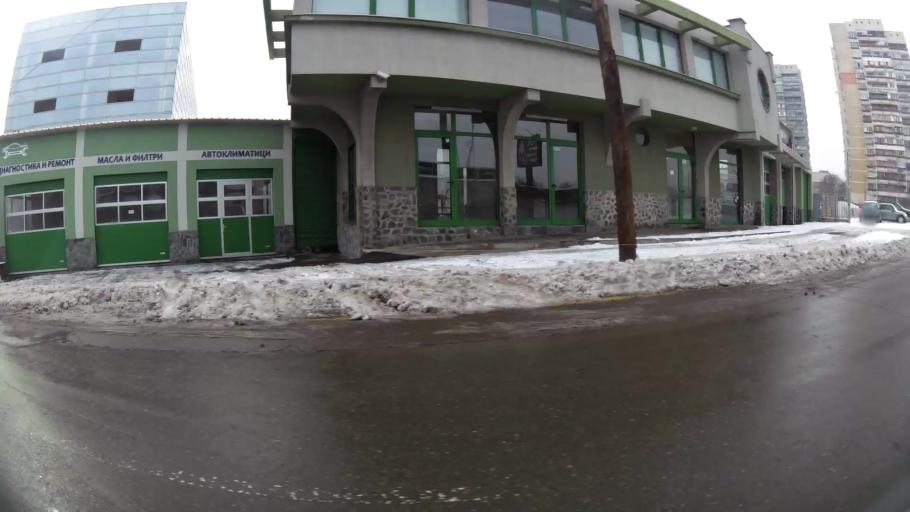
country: BG
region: Sofia-Capital
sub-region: Stolichna Obshtina
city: Sofia
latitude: 42.7097
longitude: 23.3646
